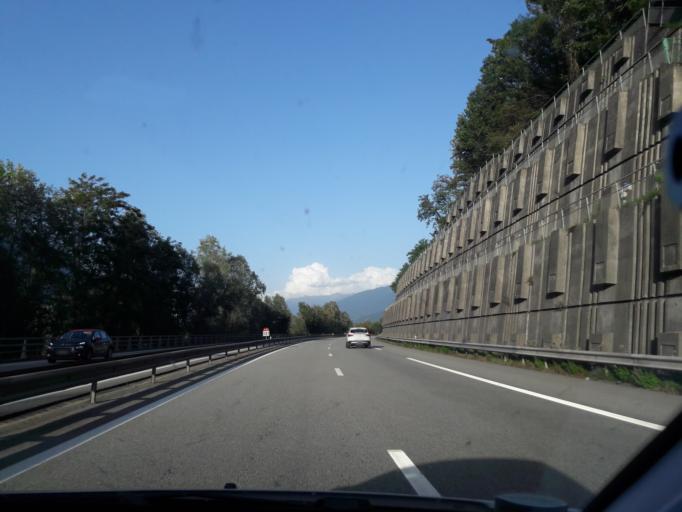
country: FR
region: Rhone-Alpes
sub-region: Departement de la Savoie
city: Coise-Saint-Jean-Pied-Gauthier
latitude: 45.5518
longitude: 6.1669
